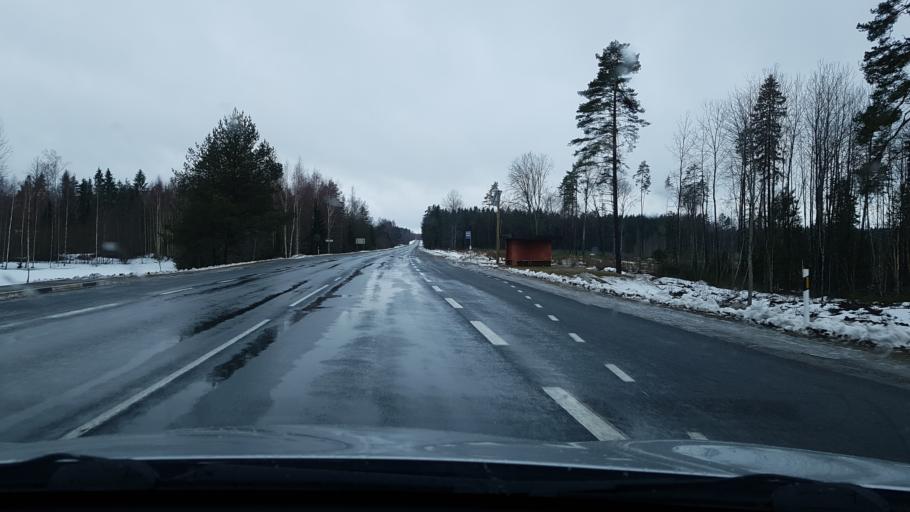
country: LV
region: Apes Novads
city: Ape
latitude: 57.7286
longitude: 26.7811
